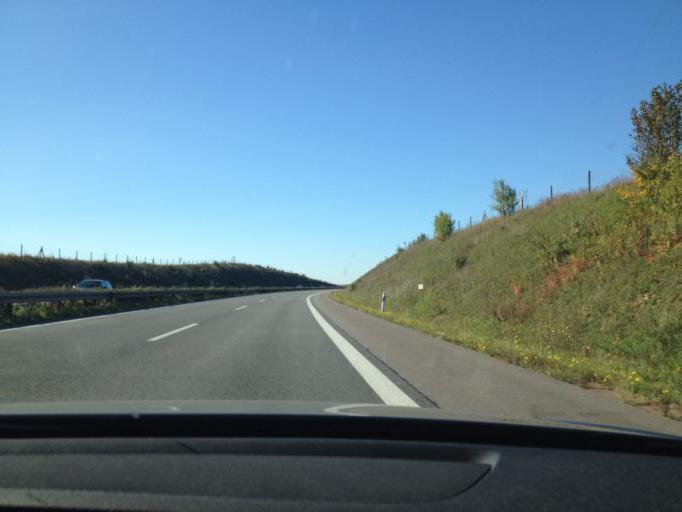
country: DE
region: Saarland
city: Perl
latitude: 49.4683
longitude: 6.4446
